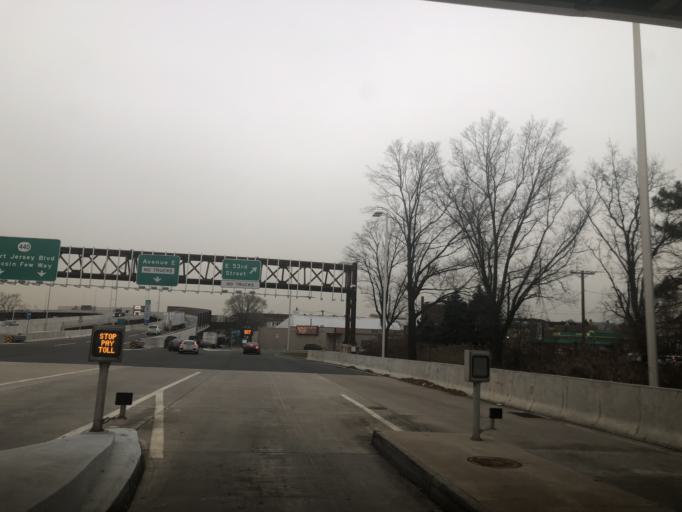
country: US
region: New Jersey
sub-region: Hudson County
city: Bayonne
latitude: 40.6841
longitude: -74.0984
